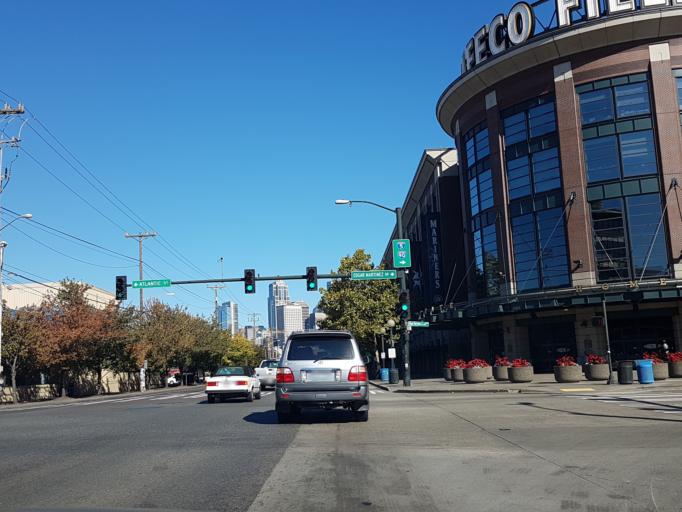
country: US
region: Washington
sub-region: King County
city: Seattle
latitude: 47.5901
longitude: -122.3341
